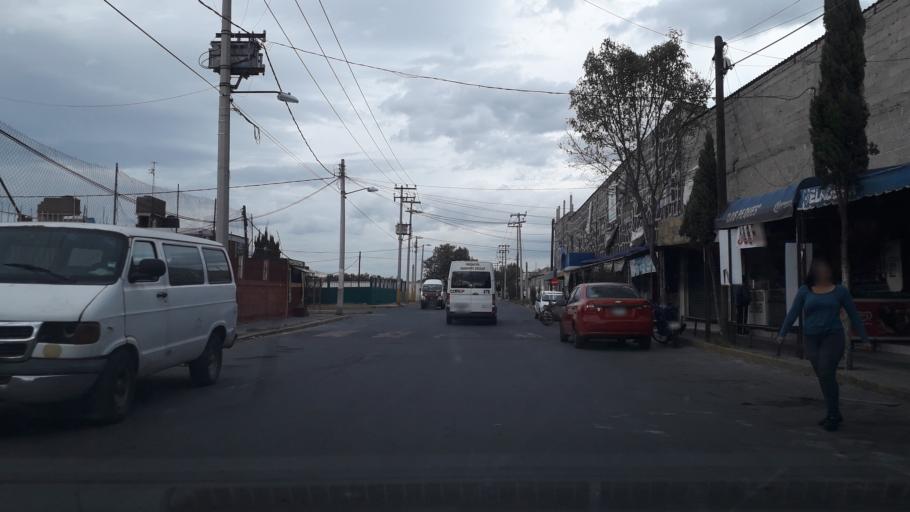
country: MX
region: Mexico
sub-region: Jaltenco
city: Alborada Jaltenco
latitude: 19.6651
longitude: -99.0703
